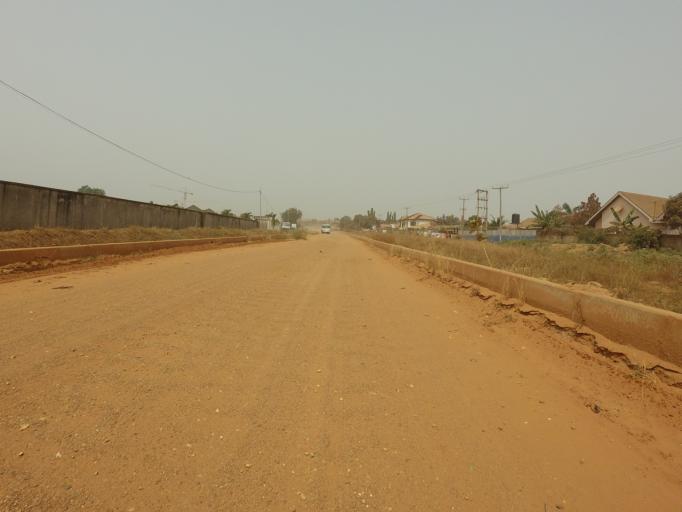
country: GH
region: Greater Accra
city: Teshi Old Town
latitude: 5.6299
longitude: -0.1243
